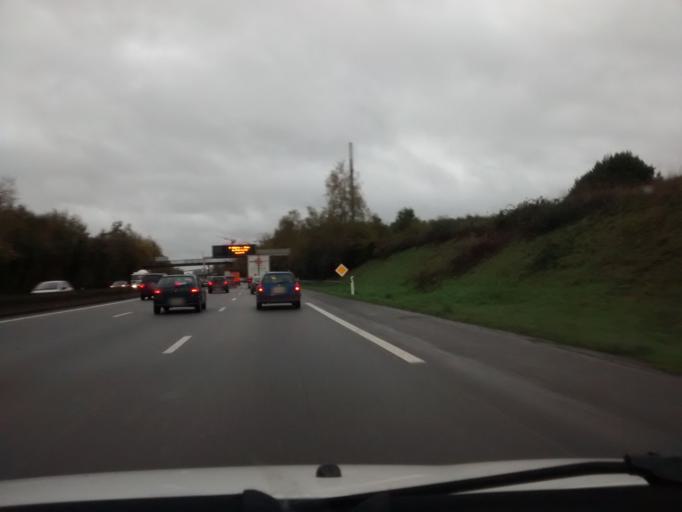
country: FR
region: Brittany
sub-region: Departement d'Ille-et-Vilaine
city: Saint-Jacques-de-la-Lande
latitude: 48.1001
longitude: -1.7150
